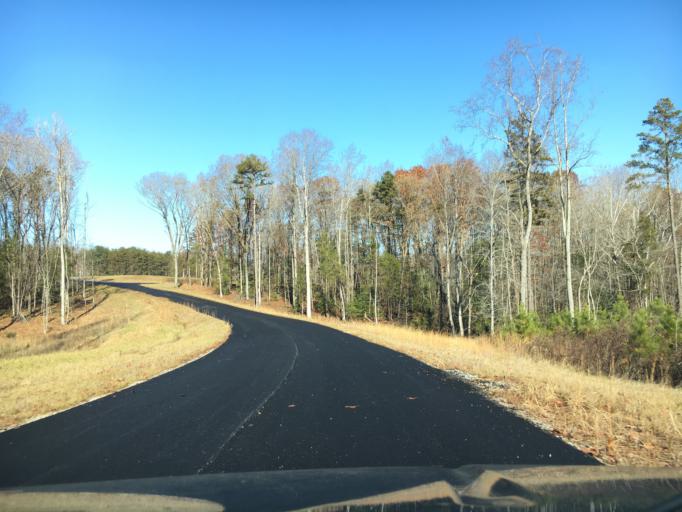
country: US
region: Virginia
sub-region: Goochland County
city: Goochland
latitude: 37.6912
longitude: -77.8390
